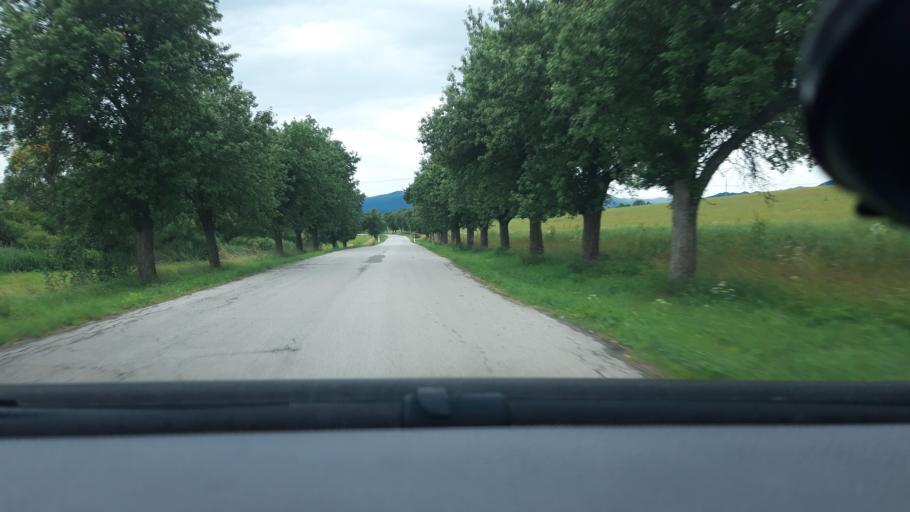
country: SK
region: Zilinsky
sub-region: Okres Martin
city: Martin
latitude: 48.9773
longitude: 18.9273
